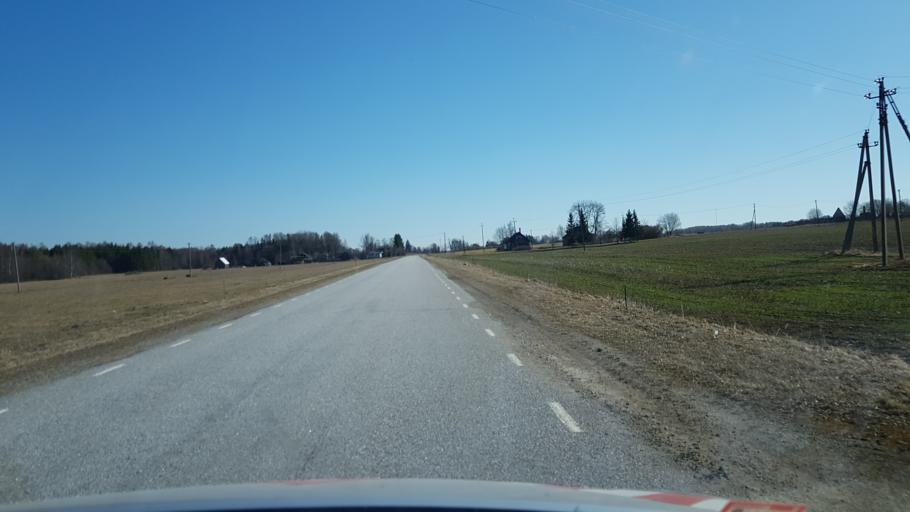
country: EE
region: Jaervamaa
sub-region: Koeru vald
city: Koeru
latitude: 59.0477
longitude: 26.0892
